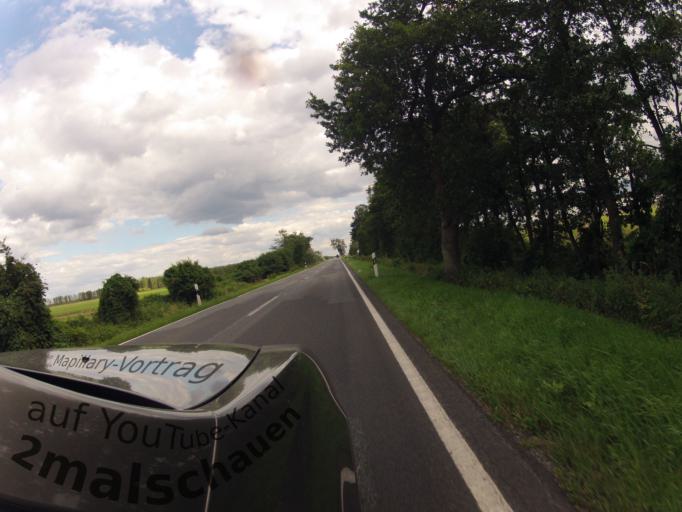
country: DE
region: Mecklenburg-Vorpommern
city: Lassan
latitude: 53.8797
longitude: 13.7974
